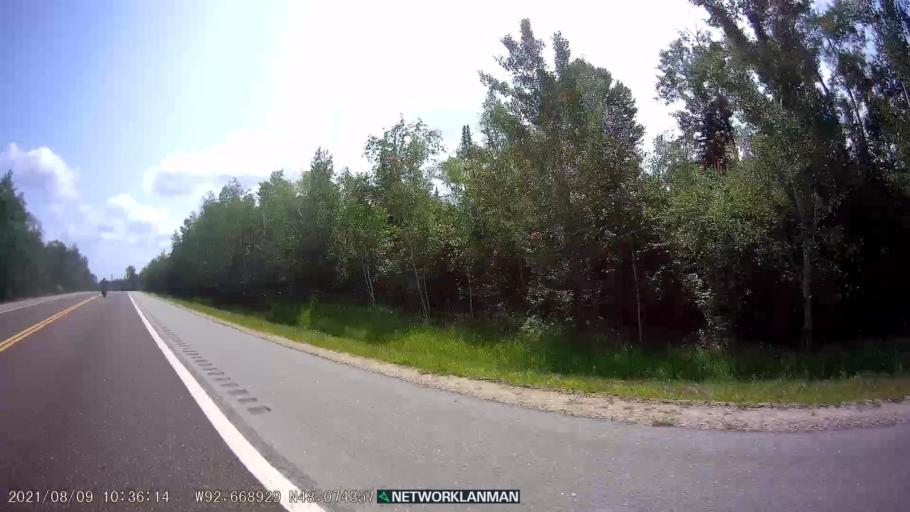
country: US
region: Minnesota
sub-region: Saint Louis County
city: Mountain Iron
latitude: 48.0747
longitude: -92.6683
